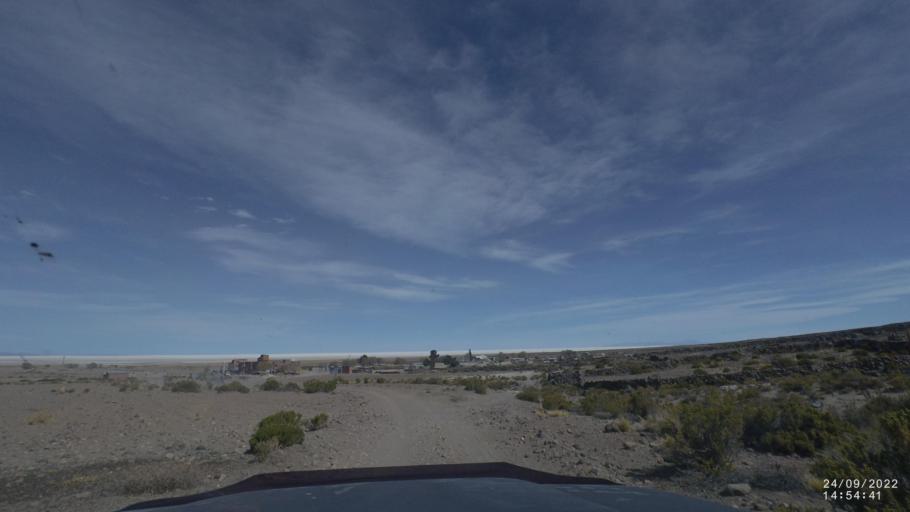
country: BO
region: Potosi
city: Colchani
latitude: -19.8545
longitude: -67.5743
